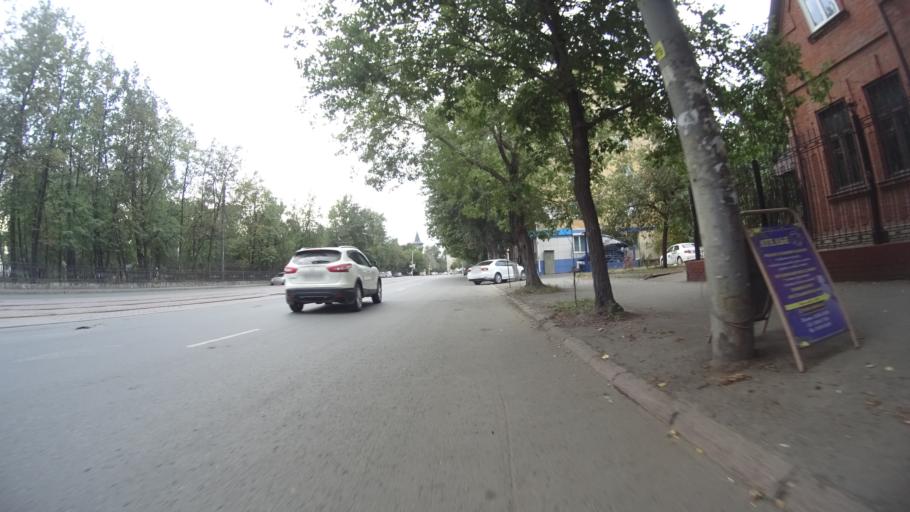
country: RU
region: Chelyabinsk
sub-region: Gorod Chelyabinsk
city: Chelyabinsk
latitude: 55.1535
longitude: 61.4087
